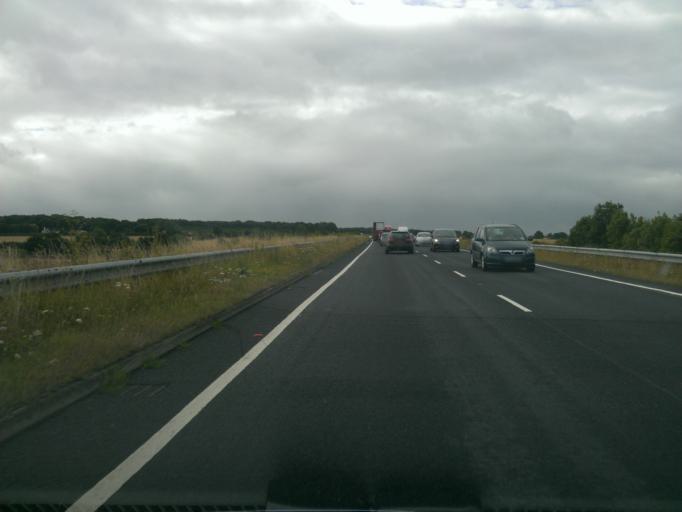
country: GB
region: England
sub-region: Essex
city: Great Bentley
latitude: 51.8550
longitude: 1.1012
